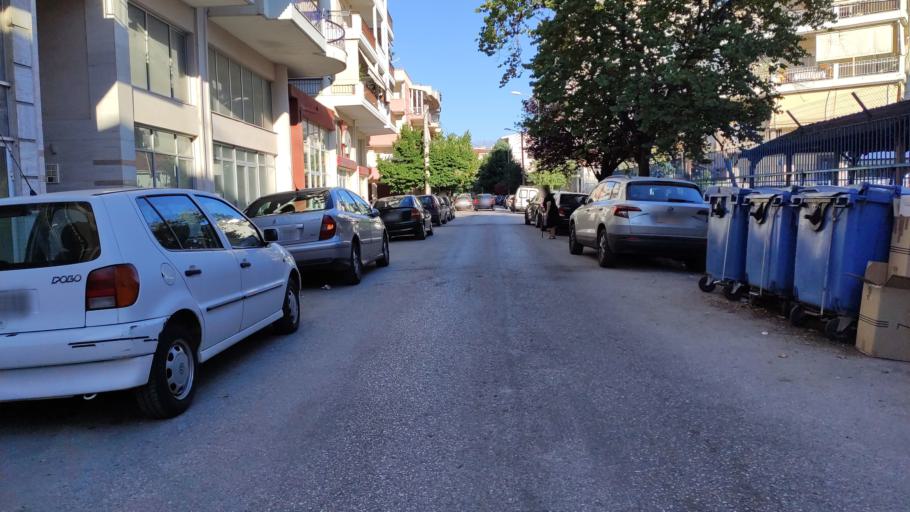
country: GR
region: East Macedonia and Thrace
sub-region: Nomos Rodopis
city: Komotini
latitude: 41.1182
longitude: 25.3942
